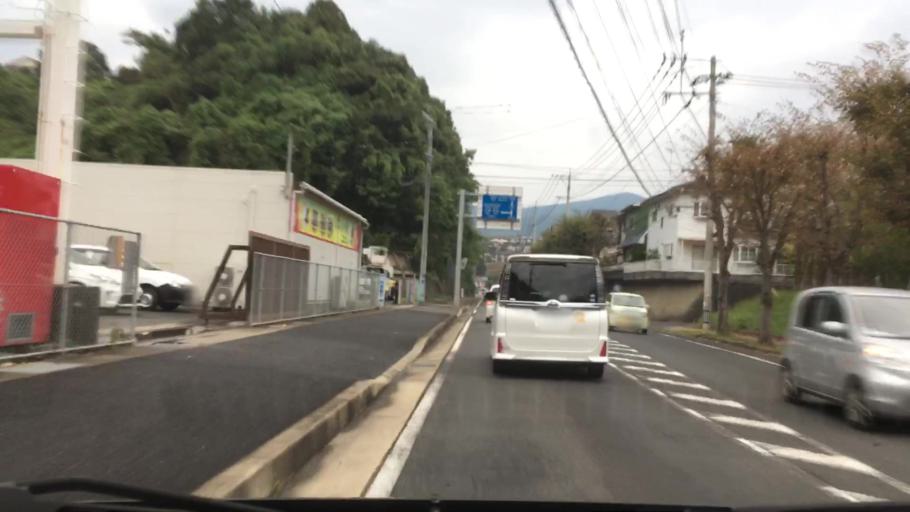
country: JP
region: Nagasaki
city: Sasebo
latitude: 33.1276
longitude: 129.7923
